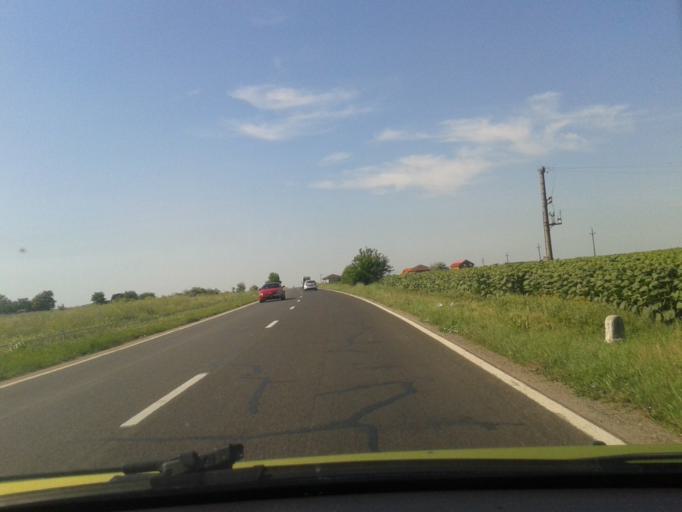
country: RO
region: Constanta
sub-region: Municipiul Mangalia
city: Mangalia
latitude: 43.7669
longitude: 28.5744
